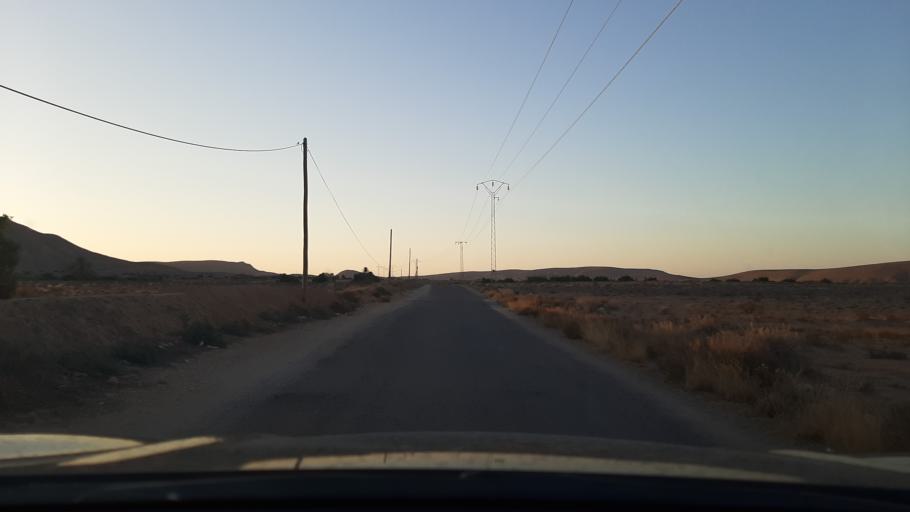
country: TN
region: Qabis
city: Matmata
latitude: 33.5460
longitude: 10.1917
